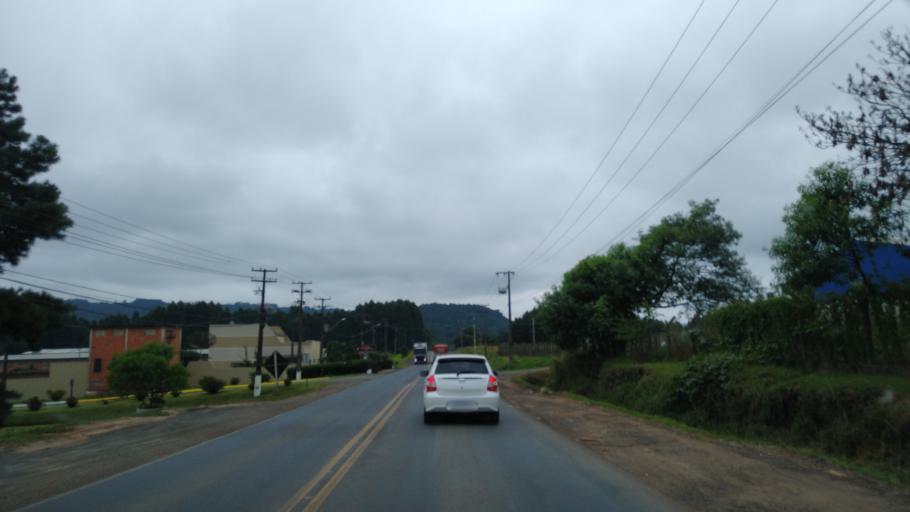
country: BR
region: Parana
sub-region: Uniao Da Vitoria
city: Uniao da Vitoria
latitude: -26.2426
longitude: -51.1231
